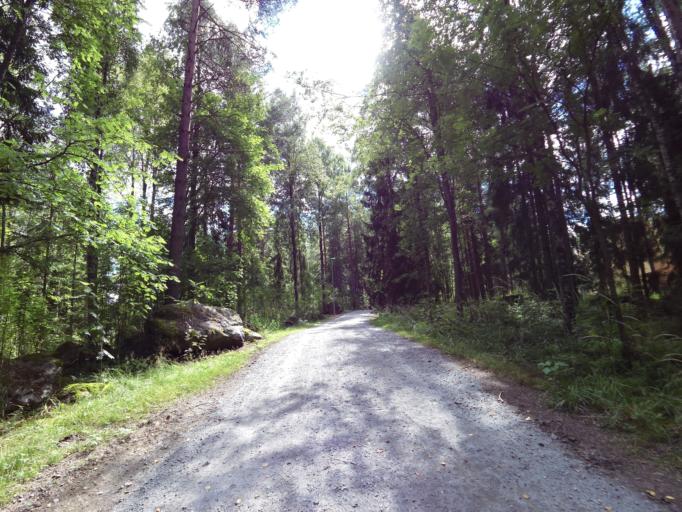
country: FI
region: Pirkanmaa
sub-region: Tampere
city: Yloejaervi
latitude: 61.5096
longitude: 23.6101
